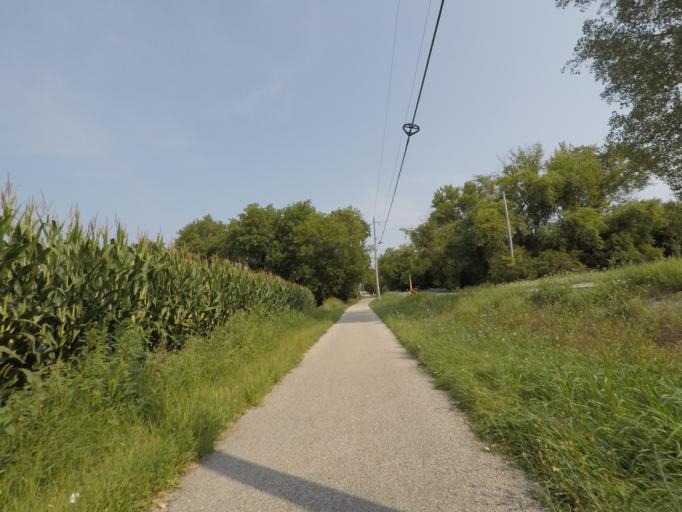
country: US
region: Wisconsin
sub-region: Waukesha County
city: Wales
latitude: 43.0191
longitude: -88.4139
